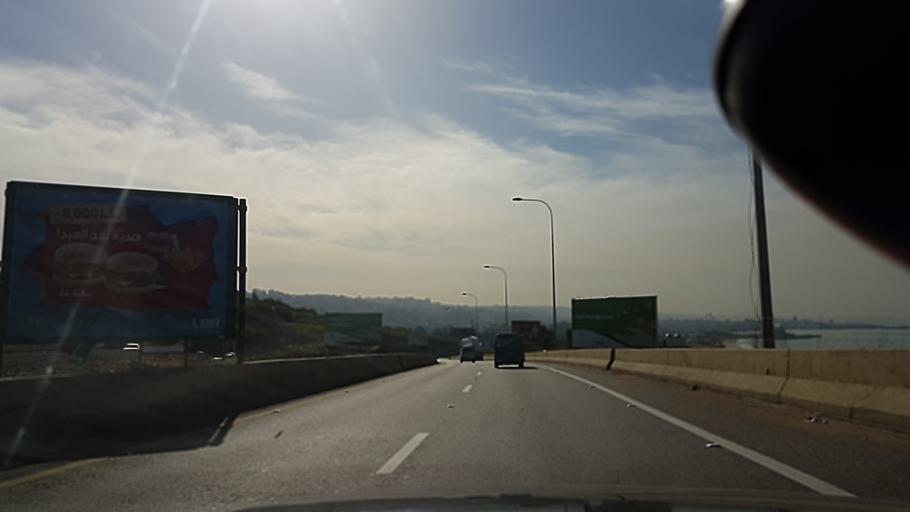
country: LB
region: Liban-Sud
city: Sidon
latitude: 33.6015
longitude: 35.3907
